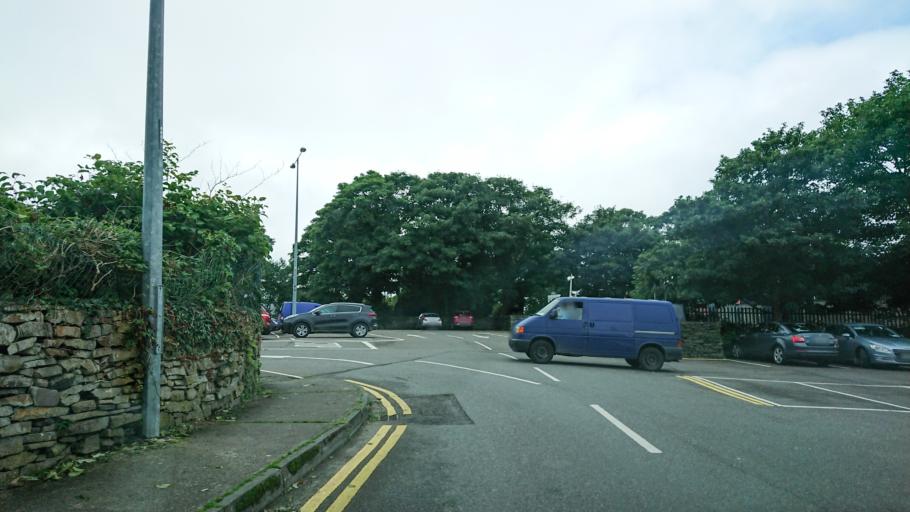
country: IE
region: Munster
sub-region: Ciarrai
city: Cahersiveen
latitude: 51.9471
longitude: -10.2270
